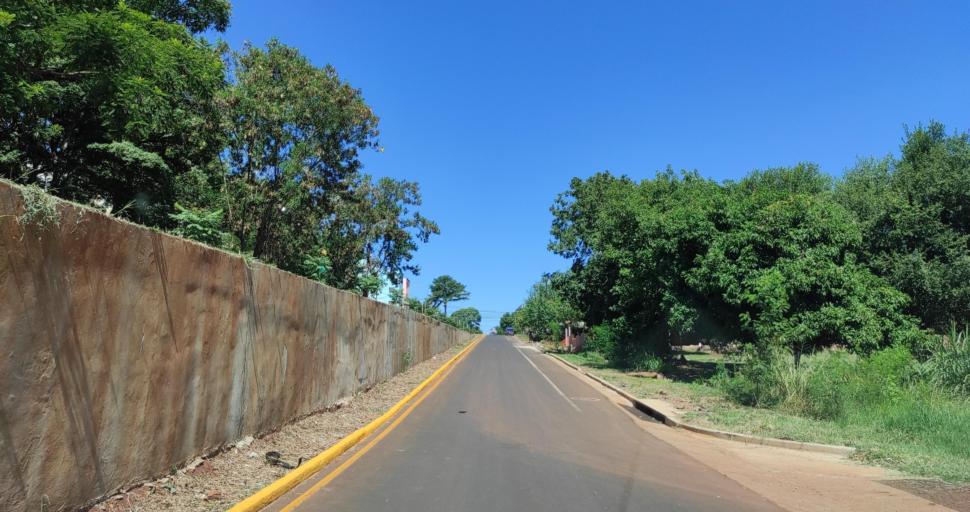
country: AR
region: Misiones
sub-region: Departamento de Capital
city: Posadas
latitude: -27.3754
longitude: -55.9500
